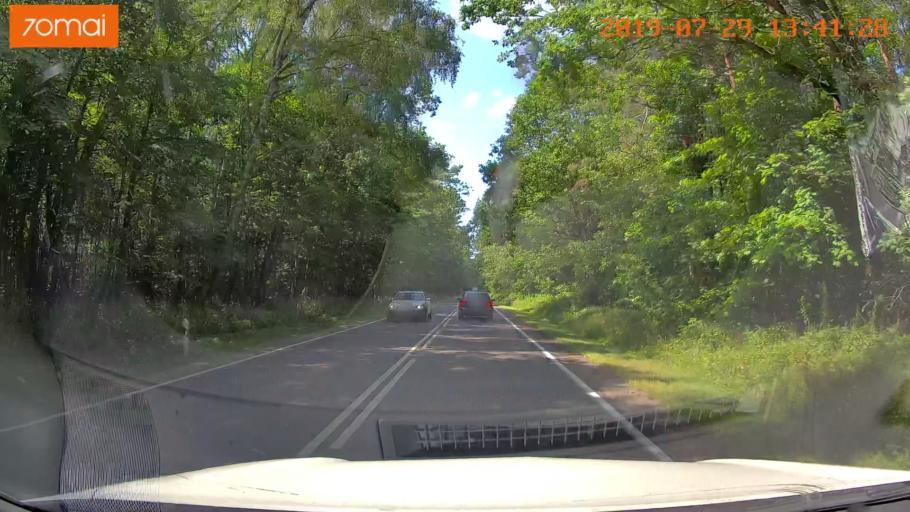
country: RU
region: Kaliningrad
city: Svetlyy
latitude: 54.7354
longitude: 20.1261
